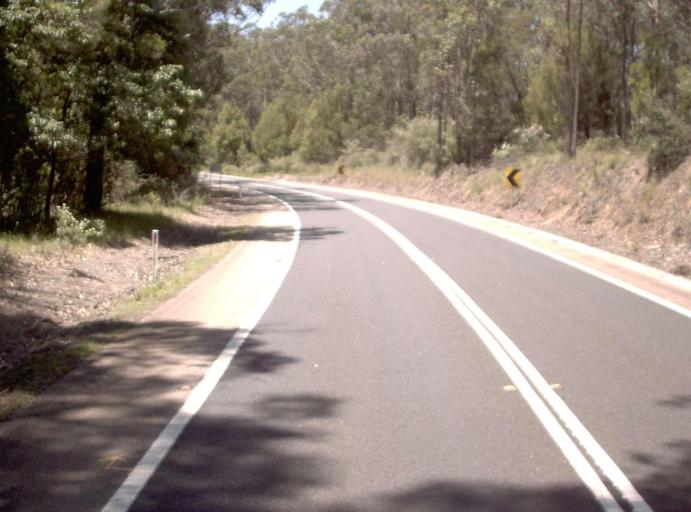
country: AU
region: Victoria
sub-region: East Gippsland
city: Lakes Entrance
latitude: -37.7064
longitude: 148.5746
